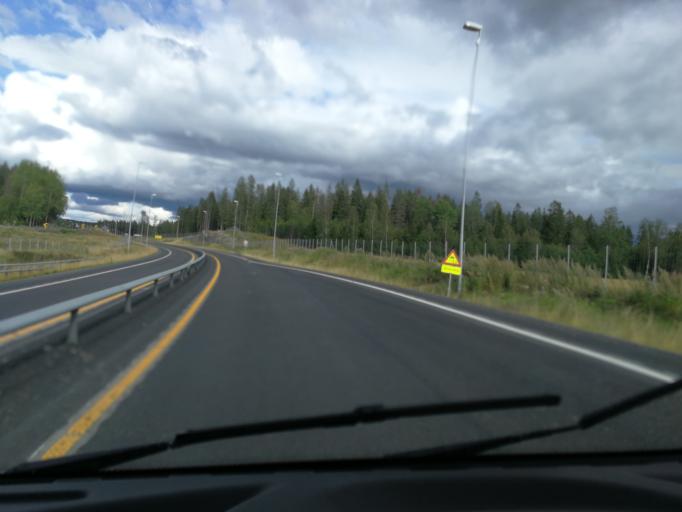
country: NO
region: Ostfold
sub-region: Marker
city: Orje
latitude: 59.4783
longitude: 11.6861
